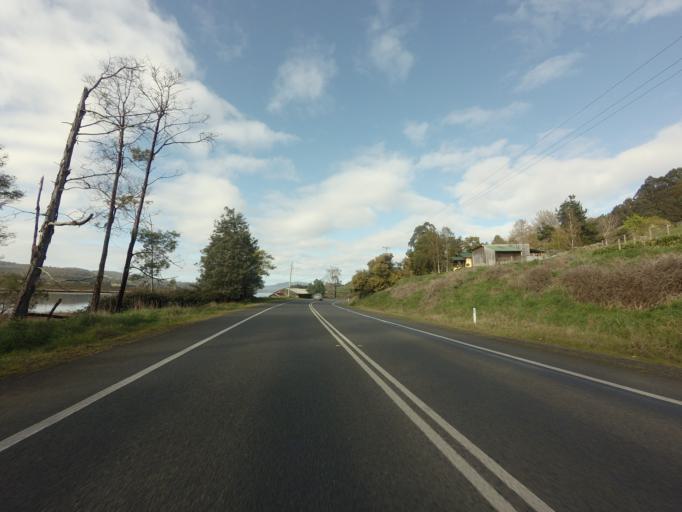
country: AU
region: Tasmania
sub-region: Huon Valley
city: Franklin
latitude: -43.1016
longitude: 147.0033
